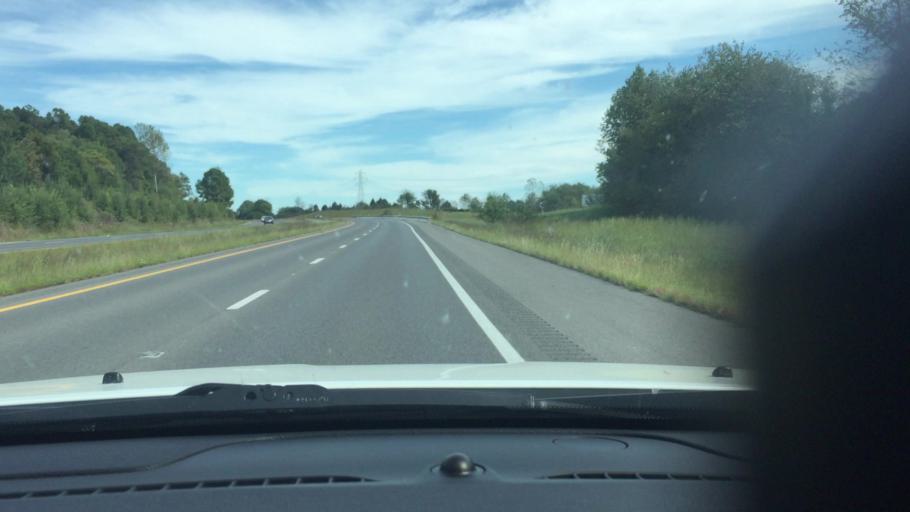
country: US
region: Kentucky
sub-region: Caldwell County
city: Princeton
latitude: 37.1099
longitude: -87.9537
